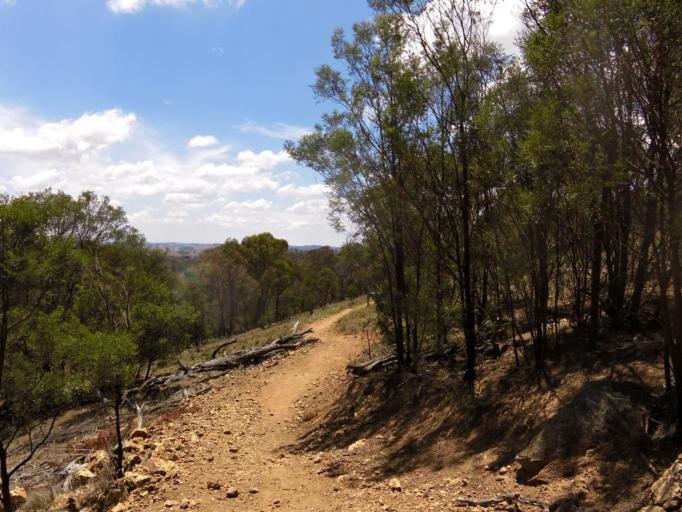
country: AU
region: Australian Capital Territory
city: Kaleen
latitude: -35.1416
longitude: 149.1471
